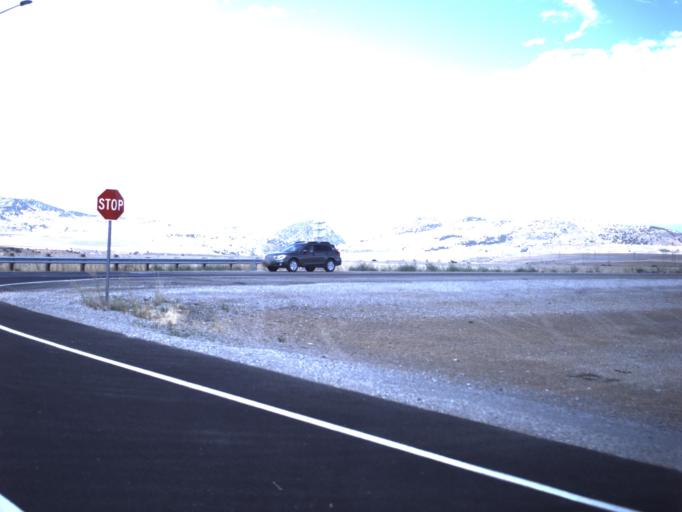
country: US
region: Utah
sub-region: Box Elder County
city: Garland
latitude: 41.7850
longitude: -112.0907
